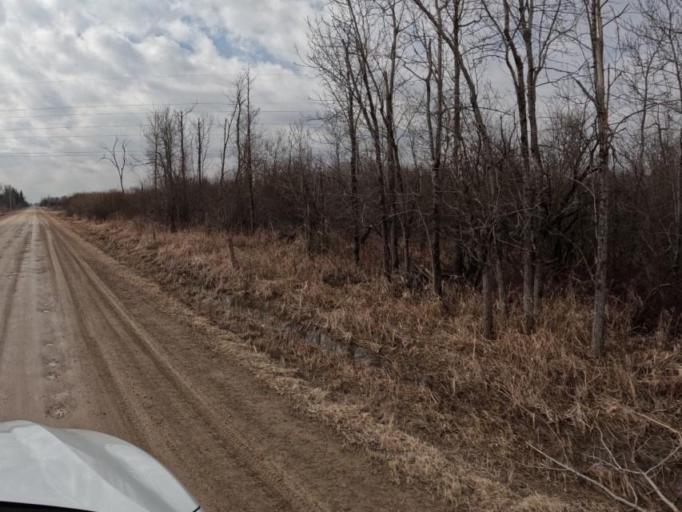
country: CA
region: Ontario
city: Orangeville
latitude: 43.9366
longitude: -80.2216
